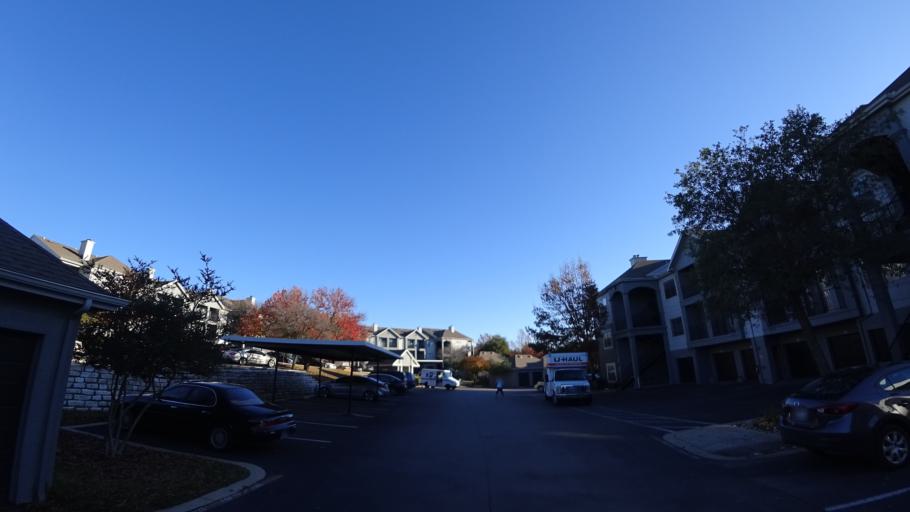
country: US
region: Texas
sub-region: Travis County
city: Wells Branch
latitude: 30.4026
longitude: -97.7066
